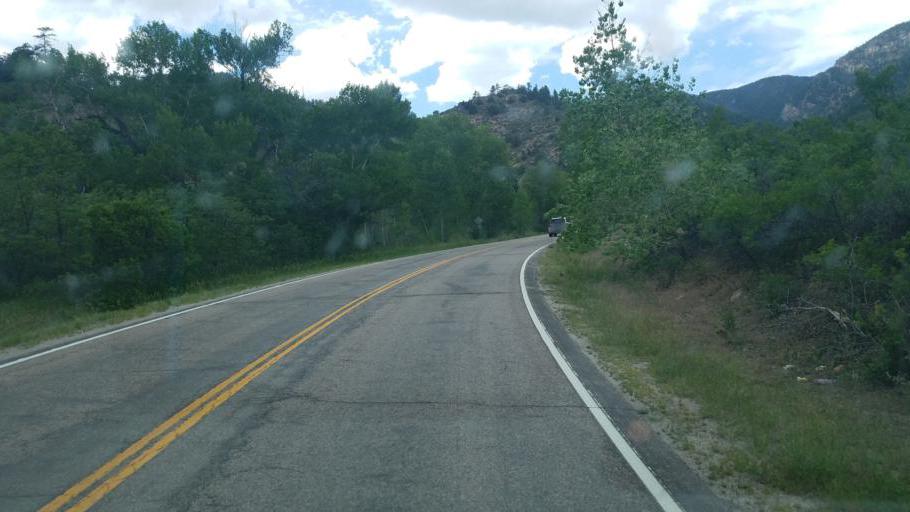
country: US
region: Colorado
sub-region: Fremont County
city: Florence
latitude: 38.1734
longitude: -105.1456
